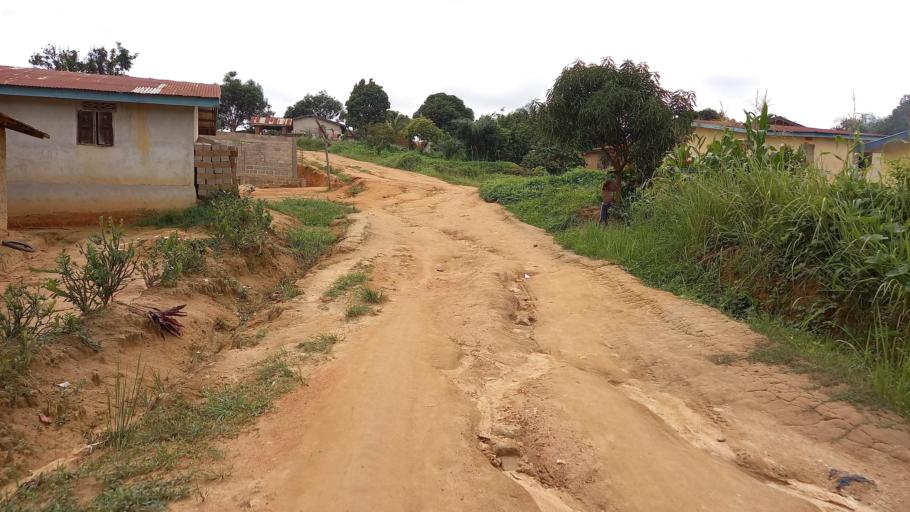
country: SL
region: Eastern Province
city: Kailahun
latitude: 8.2847
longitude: -10.5720
